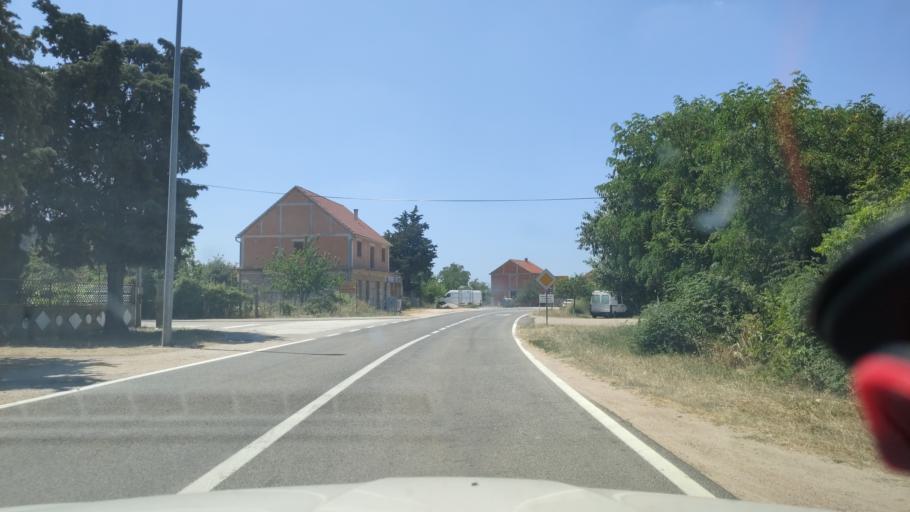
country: HR
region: Sibensko-Kniniska
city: Kistanje
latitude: 43.9838
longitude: 15.9712
